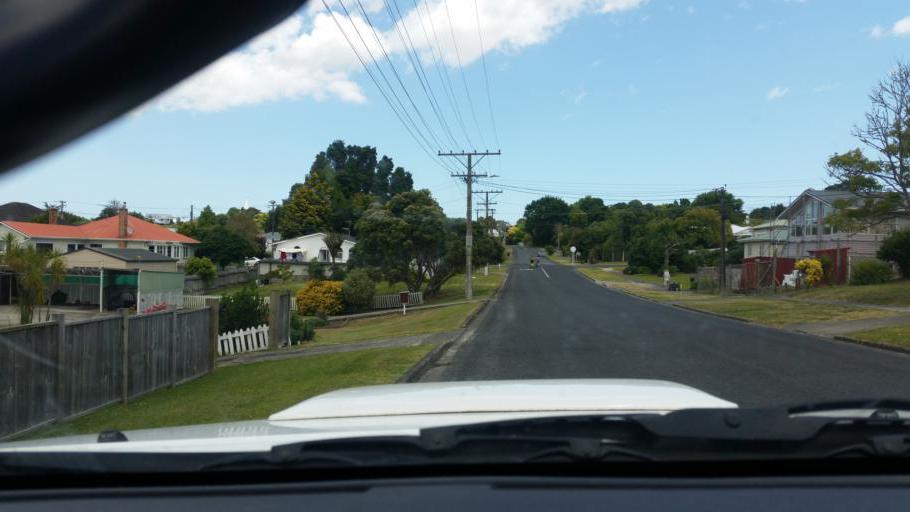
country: NZ
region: Northland
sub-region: Kaipara District
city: Dargaville
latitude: -35.9358
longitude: 173.8676
